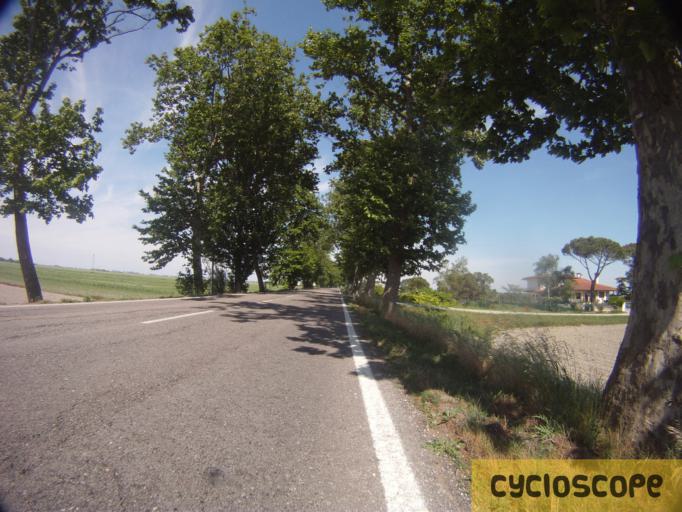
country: IT
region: Veneto
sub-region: Provincia di Venezia
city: Lugugnana
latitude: 45.7125
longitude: 12.8923
